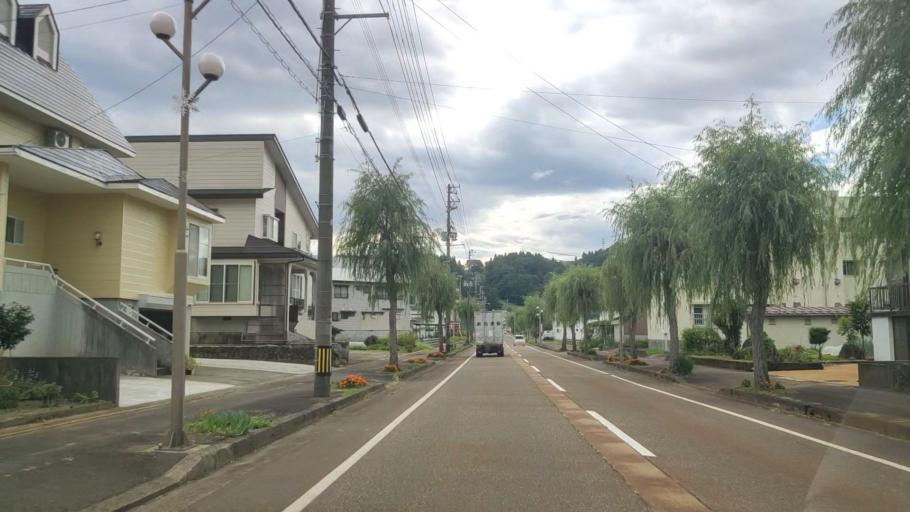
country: JP
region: Niigata
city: Arai
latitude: 37.0151
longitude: 138.2495
